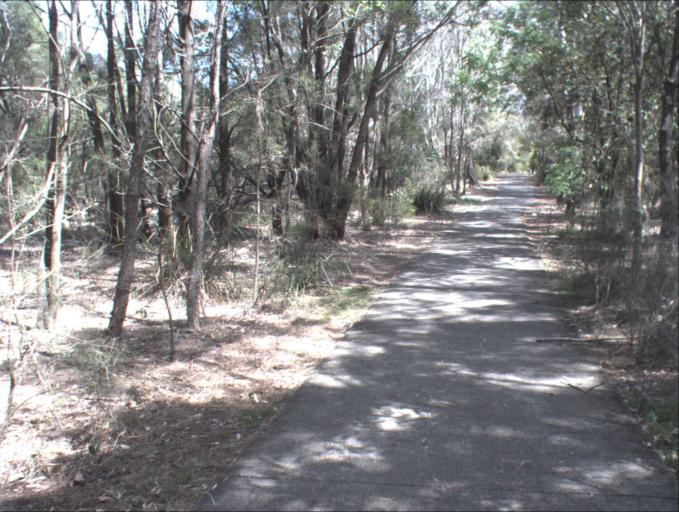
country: AU
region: Queensland
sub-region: Logan
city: Slacks Creek
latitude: -27.6716
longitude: 153.1553
